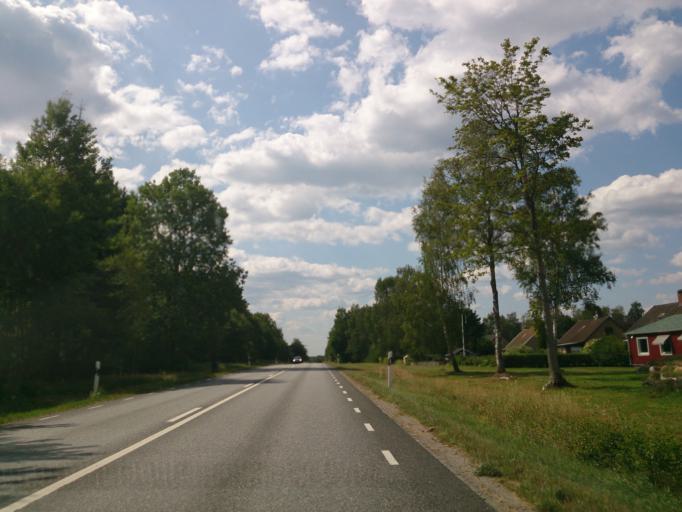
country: SE
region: Joenkoeping
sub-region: Varnamo Kommun
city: Bredaryd
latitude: 57.1734
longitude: 13.7254
